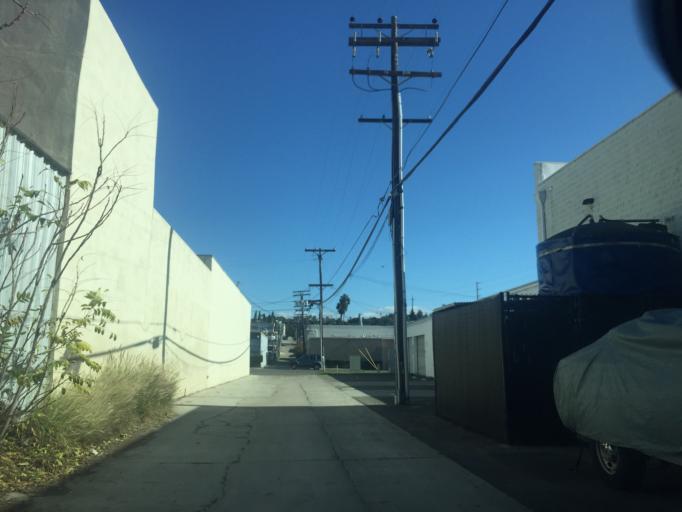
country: US
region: California
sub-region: San Diego County
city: La Mesa
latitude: 32.7882
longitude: -117.1004
